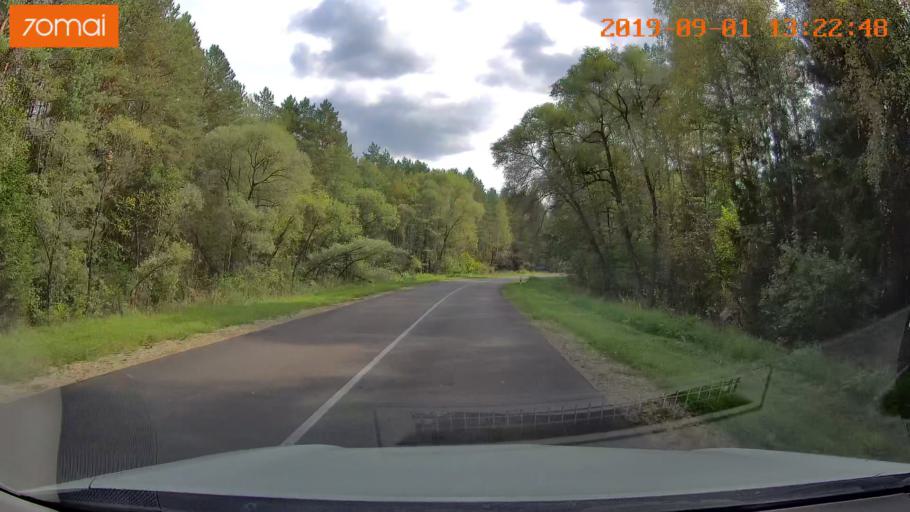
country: RU
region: Kaluga
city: Maloyaroslavets
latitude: 54.8863
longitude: 36.5281
